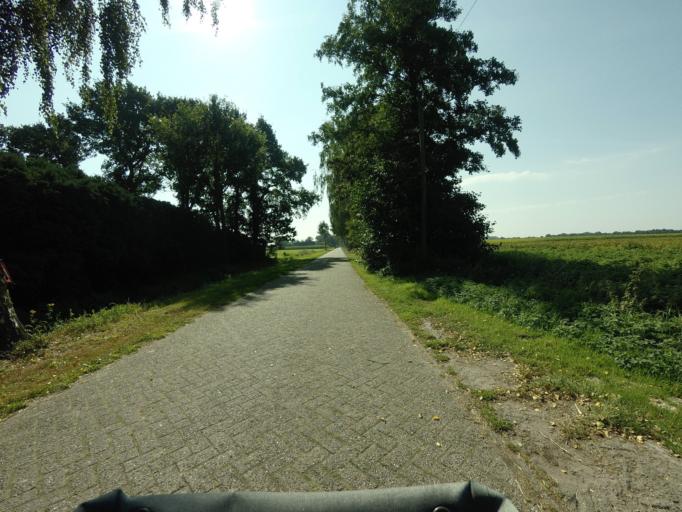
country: DE
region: Lower Saxony
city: Emlichheim
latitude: 52.5861
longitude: 6.8340
